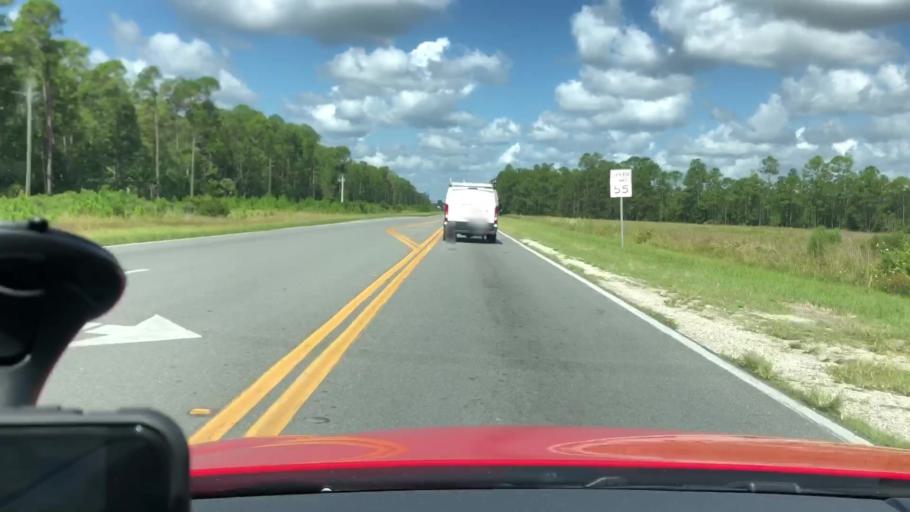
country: US
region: Florida
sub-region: Volusia County
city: Daytona Beach
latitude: 29.1529
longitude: -81.1082
